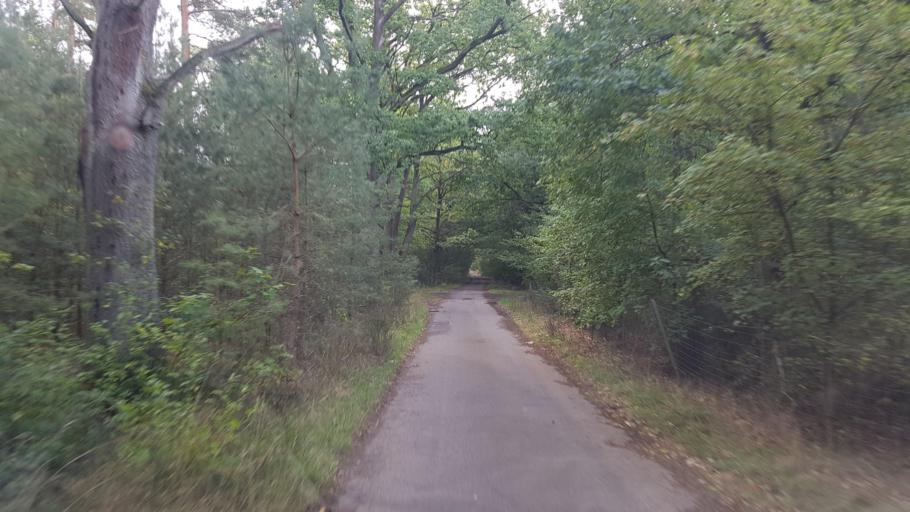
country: DE
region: Brandenburg
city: Ihlow
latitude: 51.8738
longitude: 13.2487
